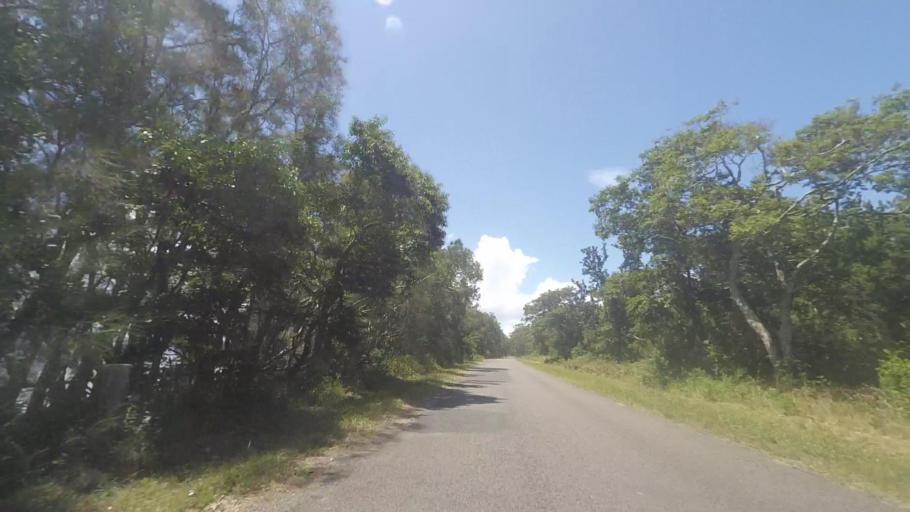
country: AU
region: New South Wales
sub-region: Great Lakes
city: Bulahdelah
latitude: -32.5342
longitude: 152.3207
